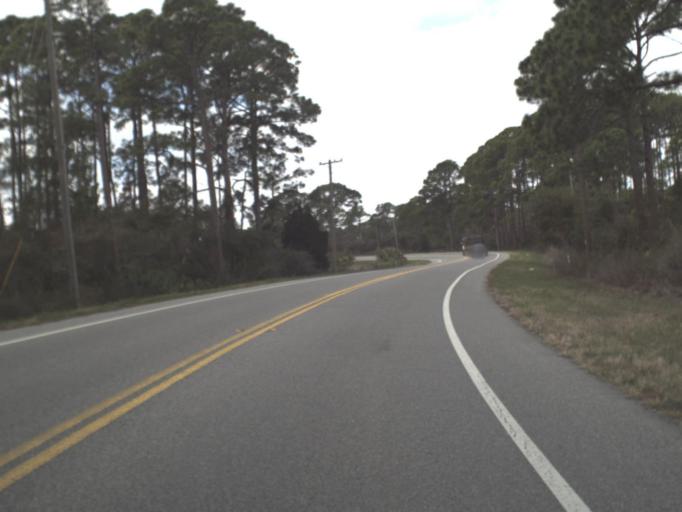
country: US
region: Florida
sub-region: Franklin County
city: Carrabelle
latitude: 29.7929
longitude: -84.7527
